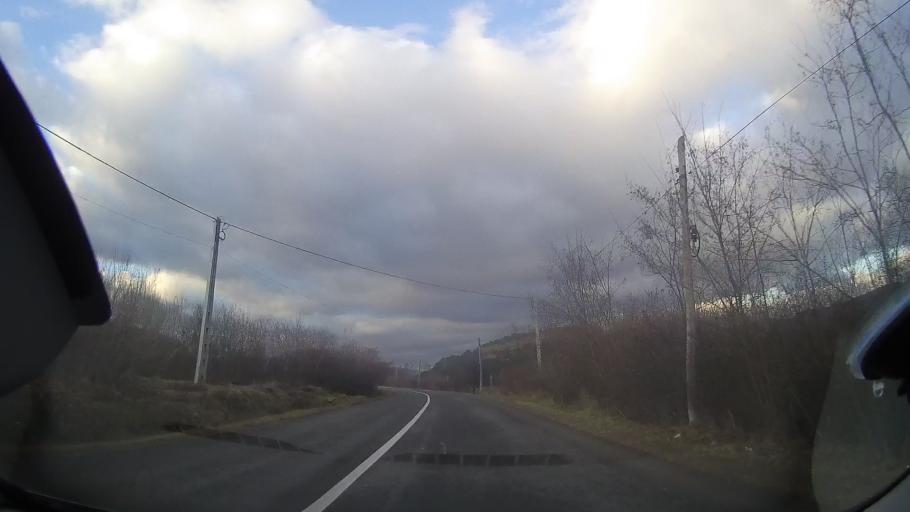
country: RO
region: Cluj
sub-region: Comuna Calatele
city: Calatele
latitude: 46.7821
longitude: 23.0051
